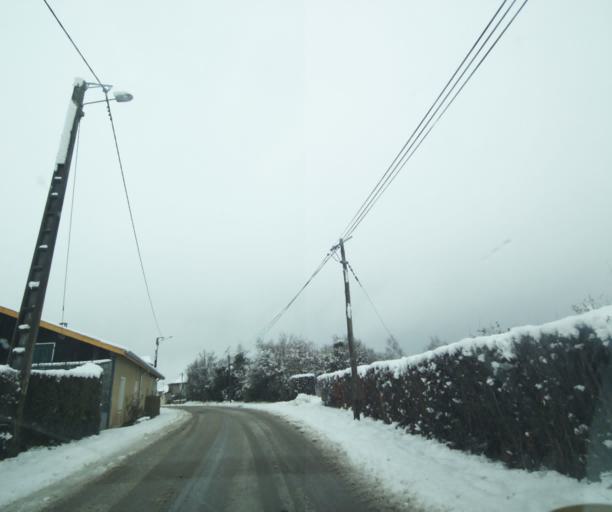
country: FR
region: Champagne-Ardenne
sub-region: Departement de la Haute-Marne
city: Montier-en-Der
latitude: 48.5090
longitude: 4.7822
